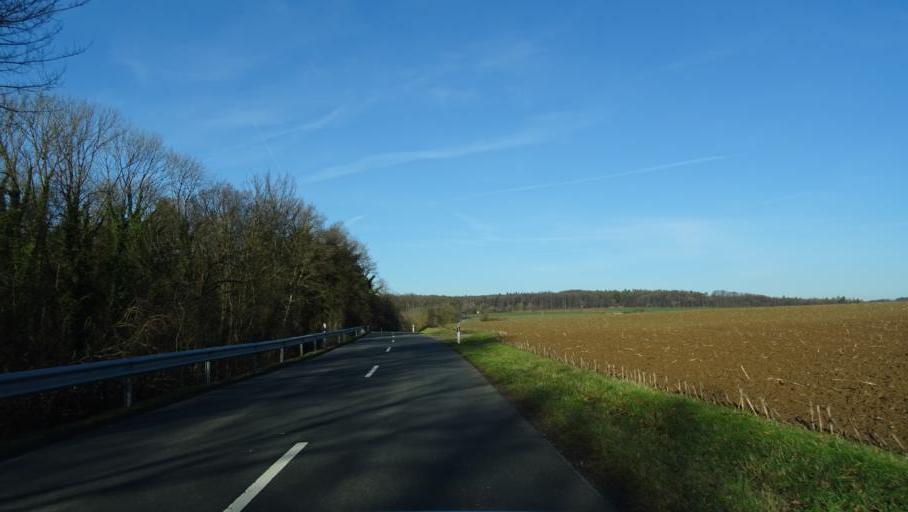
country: DE
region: Baden-Wuerttemberg
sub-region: Karlsruhe Region
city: Obrigheim
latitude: 49.3683
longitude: 9.1142
